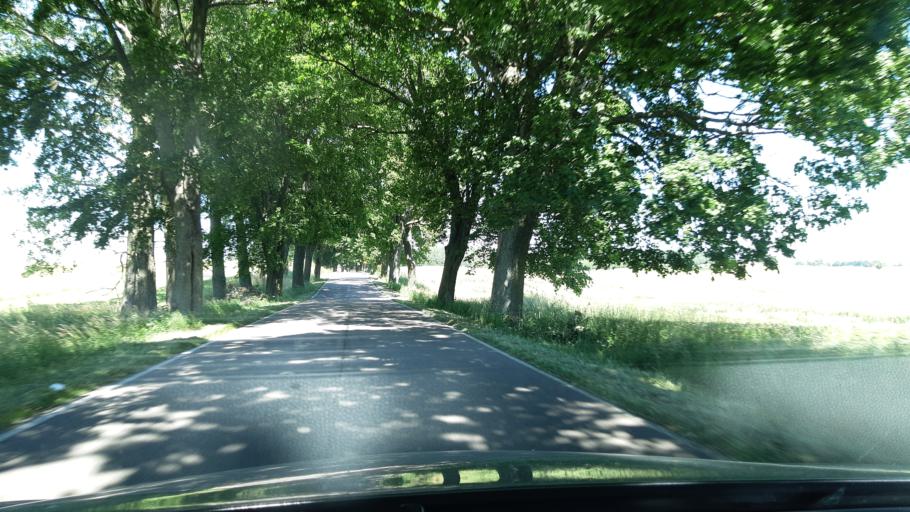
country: PL
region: Warmian-Masurian Voivodeship
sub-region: Powiat mragowski
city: Mikolajki
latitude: 53.8719
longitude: 21.6526
